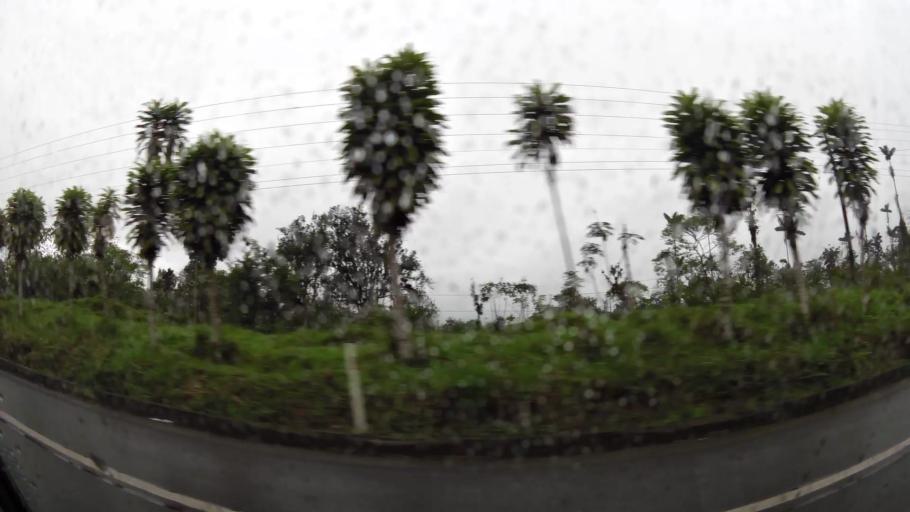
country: EC
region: Santo Domingo de los Tsachilas
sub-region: Canton Santo Domingo de los Colorados
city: Santo Domingo de los Colorados
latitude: -0.2219
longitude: -79.1230
